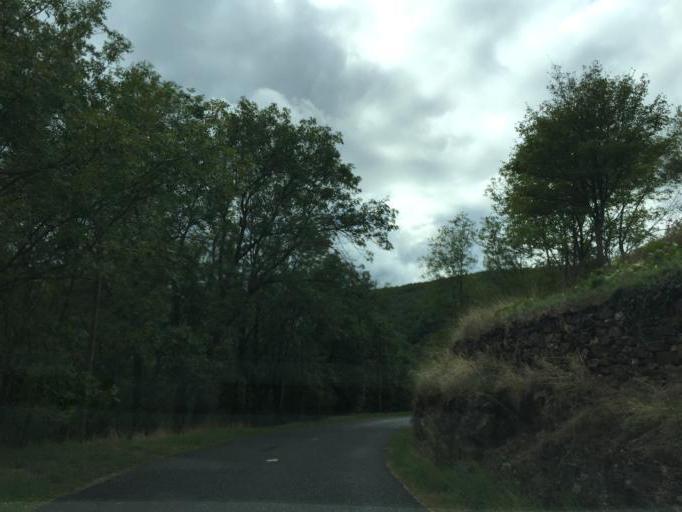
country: FR
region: Rhone-Alpes
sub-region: Departement de la Loire
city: Chateauneuf
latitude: 45.4805
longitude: 4.6433
